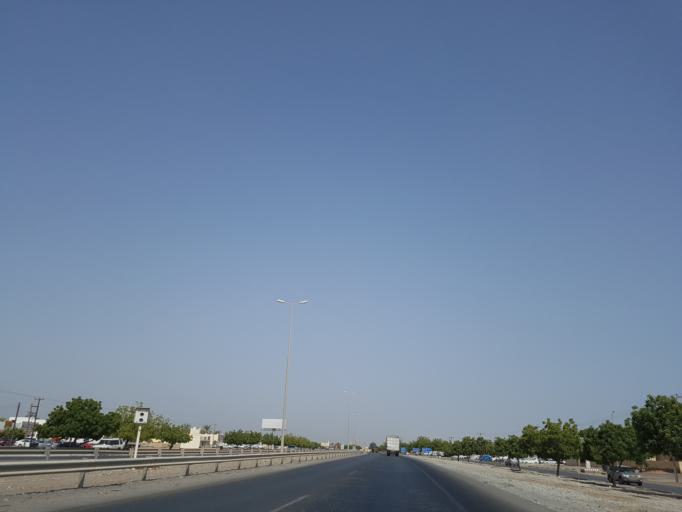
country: OM
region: Al Batinah
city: As Suwayq
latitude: 23.7527
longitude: 57.6105
